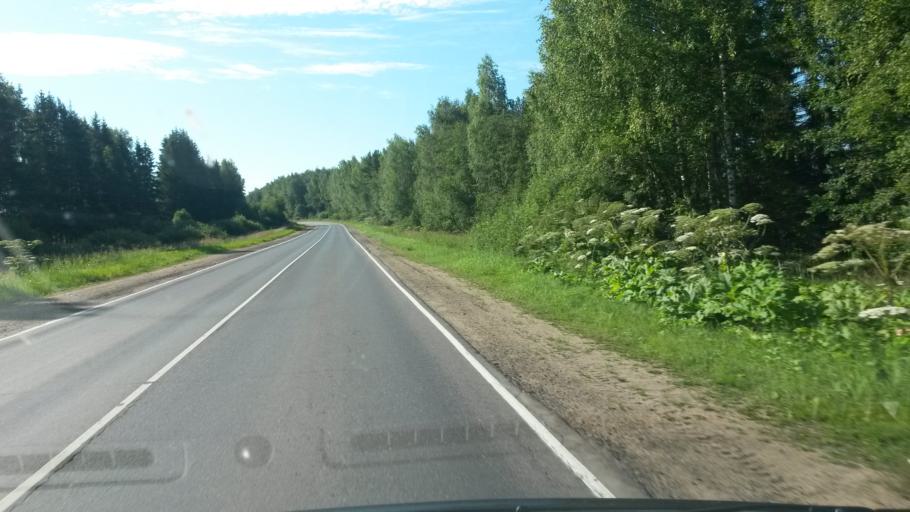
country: RU
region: Ivanovo
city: Pistsovo
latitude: 57.0939
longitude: 40.6612
